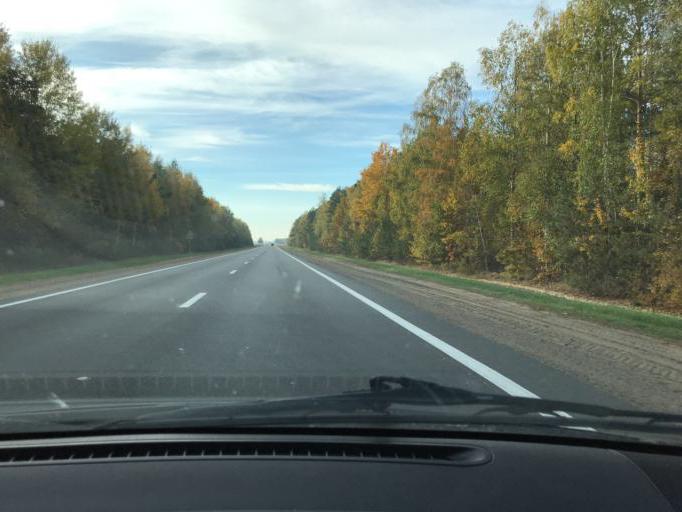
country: BY
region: Brest
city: Ivanava
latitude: 52.1565
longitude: 25.7328
